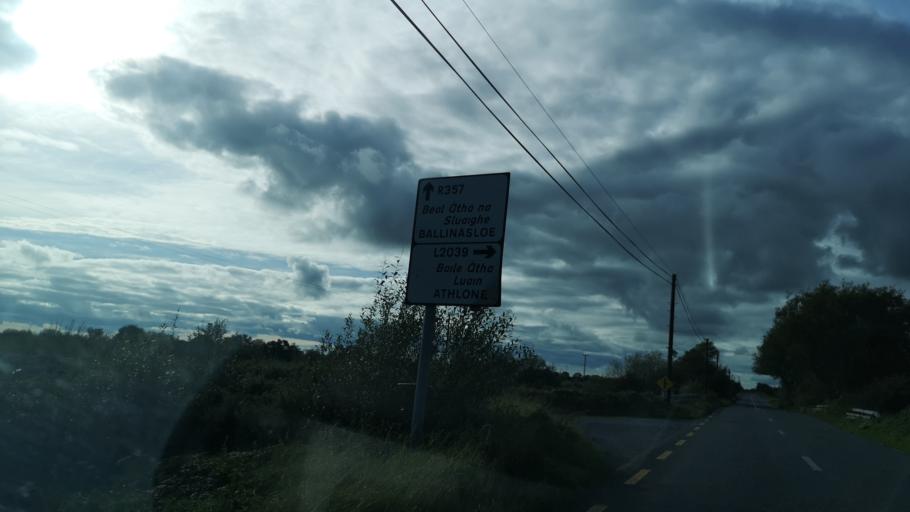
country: IE
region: Leinster
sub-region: Uibh Fhaili
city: Banagher
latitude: 53.2867
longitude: -8.0808
